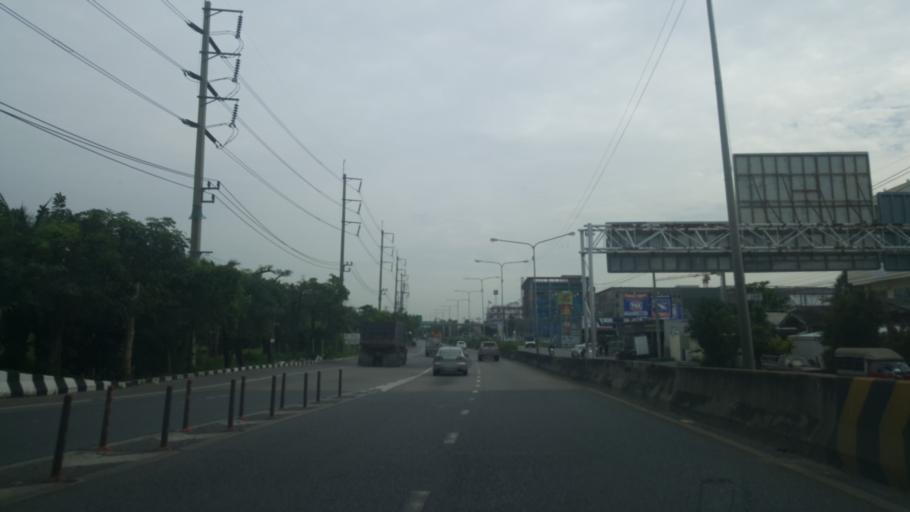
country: TH
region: Bangkok
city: Bang Khae
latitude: 13.6888
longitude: 100.4302
